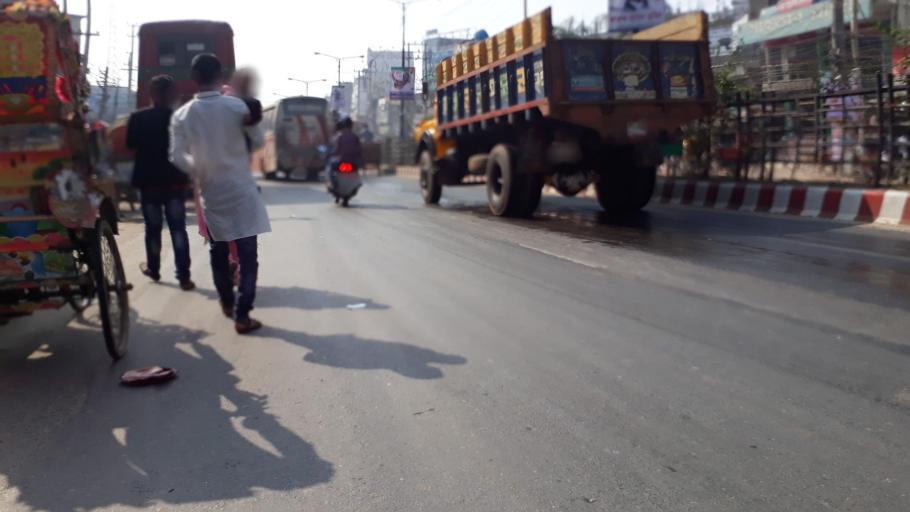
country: BD
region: Dhaka
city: Tungi
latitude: 23.8488
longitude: 90.2581
